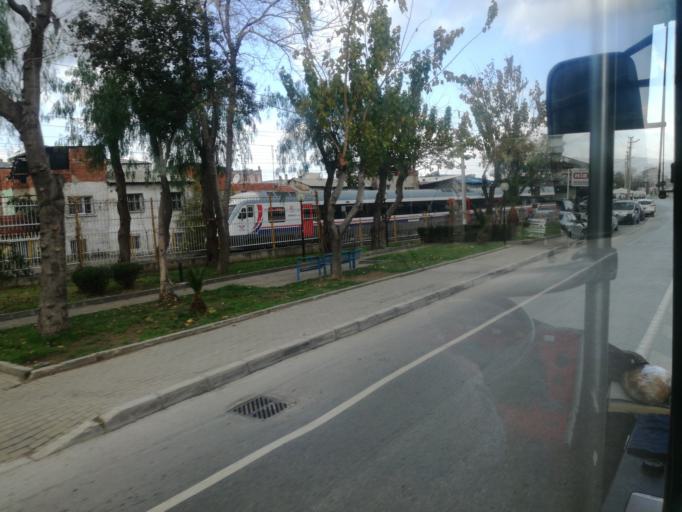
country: TR
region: Izmir
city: Buca
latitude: 38.4172
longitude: 27.1586
